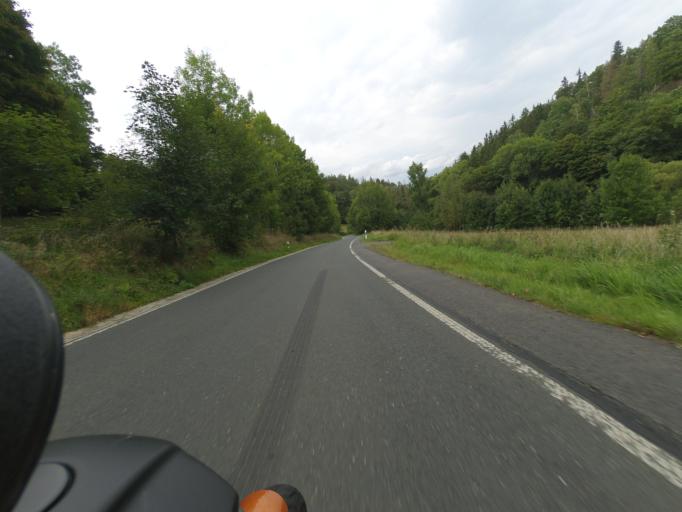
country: DE
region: Saxony
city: Glashutte
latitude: 50.8451
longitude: 13.7977
